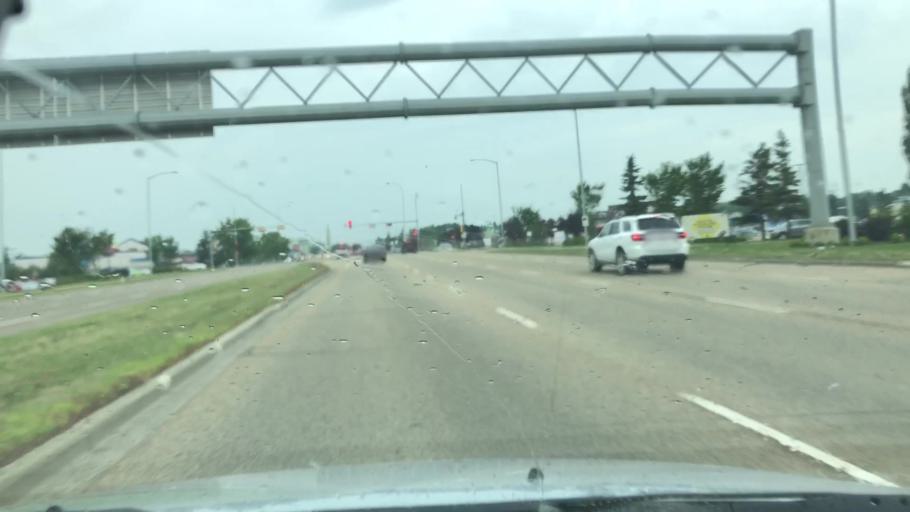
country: CA
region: Alberta
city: St. Albert
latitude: 53.6190
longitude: -113.6045
